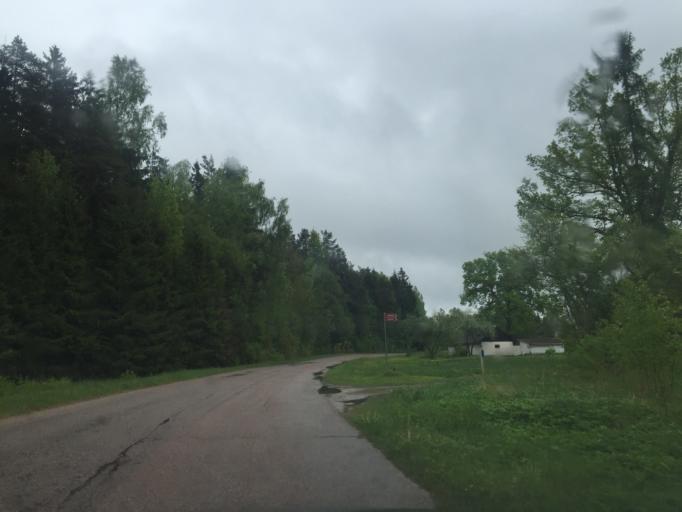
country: LV
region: Ogre
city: Jumprava
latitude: 56.6770
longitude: 24.9843
